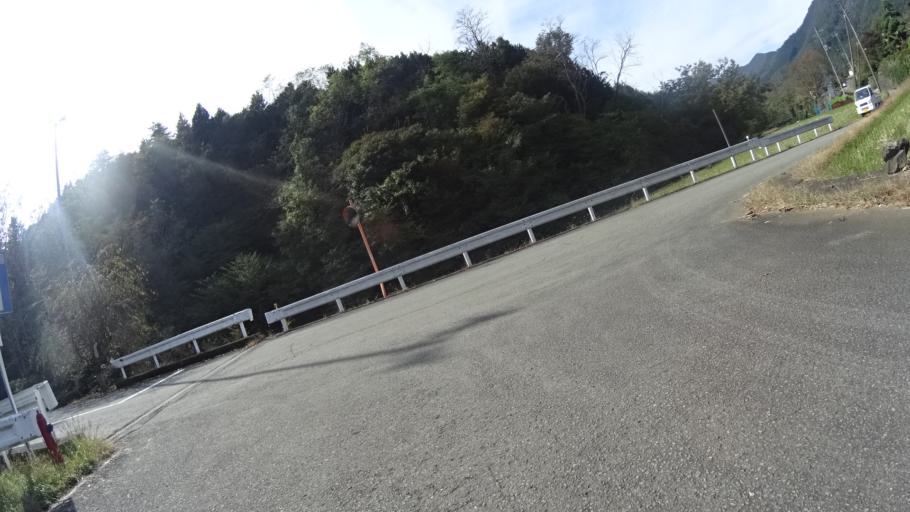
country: JP
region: Yamanashi
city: Otsuki
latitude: 35.5705
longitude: 138.9927
